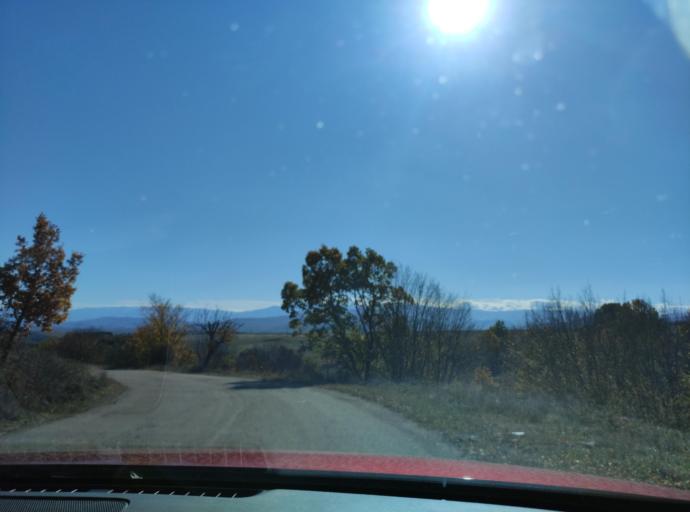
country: BG
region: Montana
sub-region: Obshtina Chiprovtsi
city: Chiprovtsi
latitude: 43.4458
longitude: 23.0472
